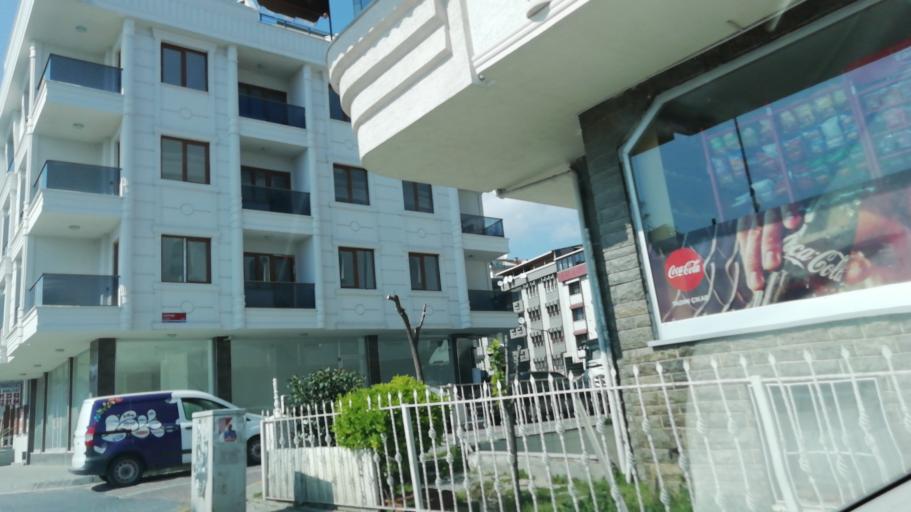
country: TR
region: Istanbul
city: Yakuplu
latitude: 40.9730
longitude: 28.7349
